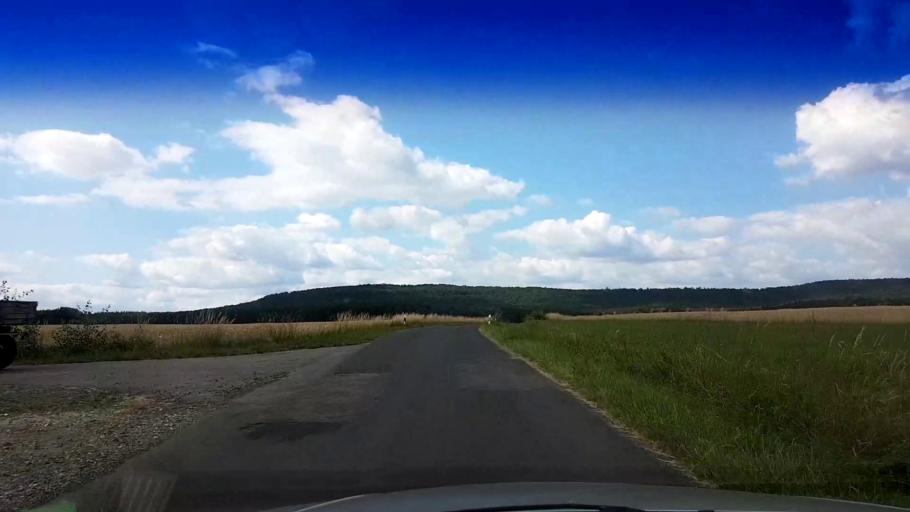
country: DE
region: Bavaria
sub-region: Upper Franconia
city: Lauter
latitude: 49.9969
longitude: 10.7689
